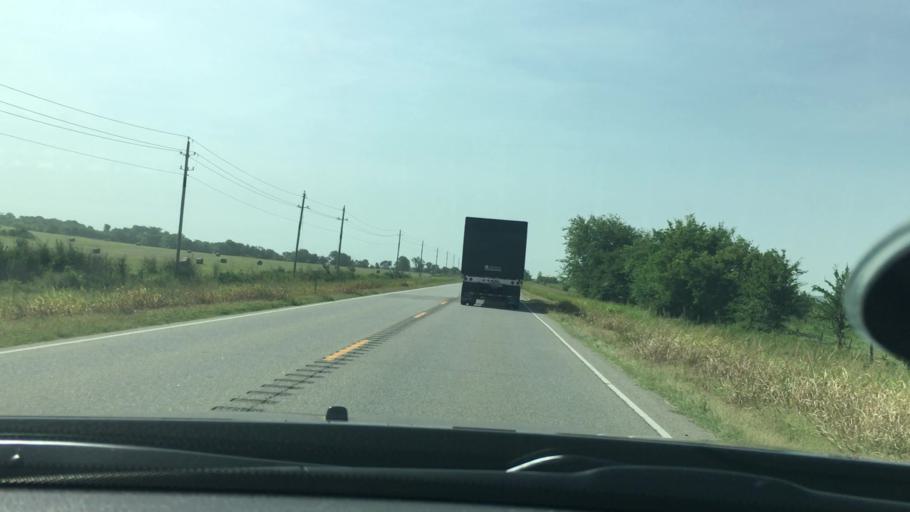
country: US
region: Oklahoma
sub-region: Atoka County
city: Atoka
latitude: 34.4318
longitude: -96.1981
